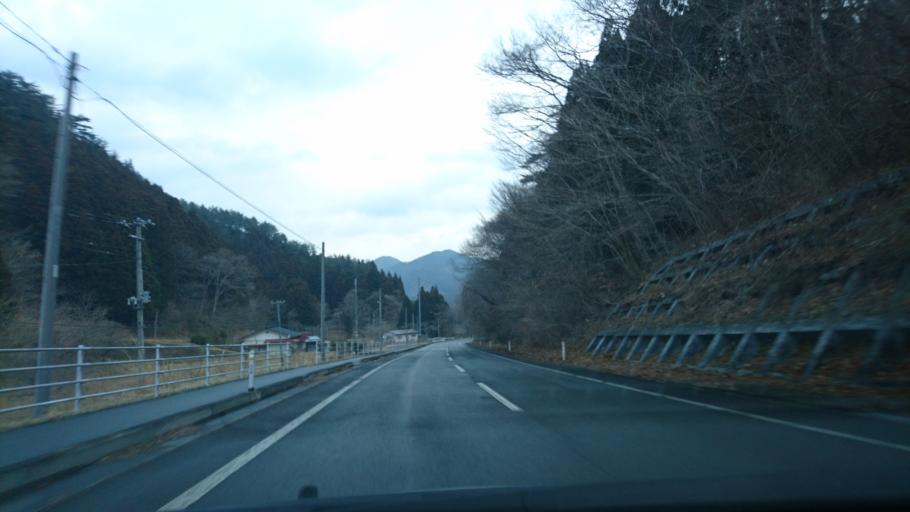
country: JP
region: Iwate
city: Ofunato
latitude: 39.0092
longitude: 141.5446
